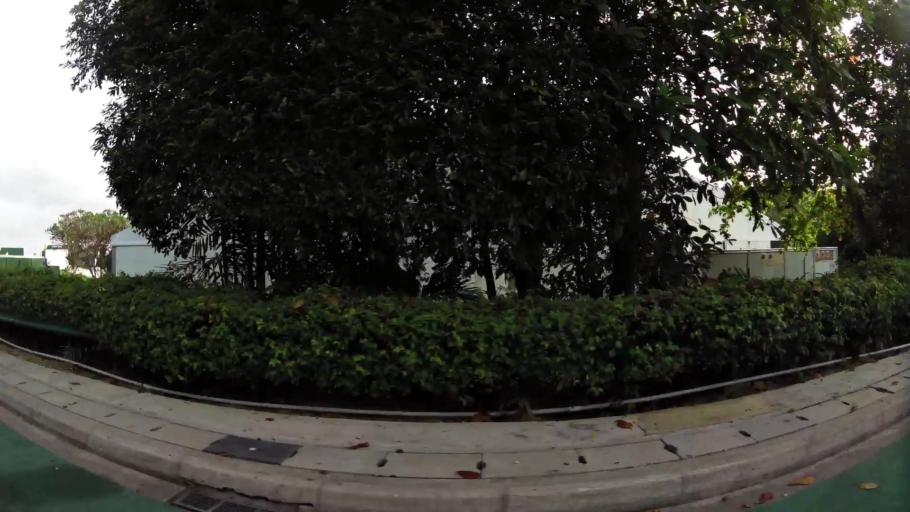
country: SG
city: Singapore
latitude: 1.2484
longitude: 103.8290
